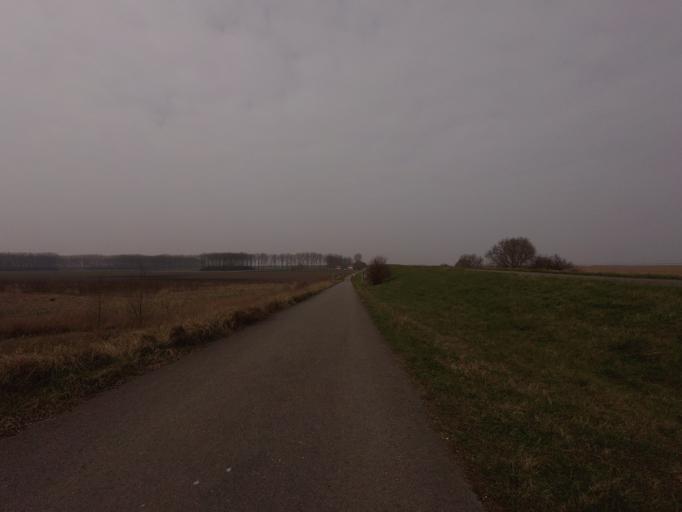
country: NL
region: North Brabant
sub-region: Gemeente Woensdrecht
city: Woensdrecht
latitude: 51.3449
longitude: 4.2333
